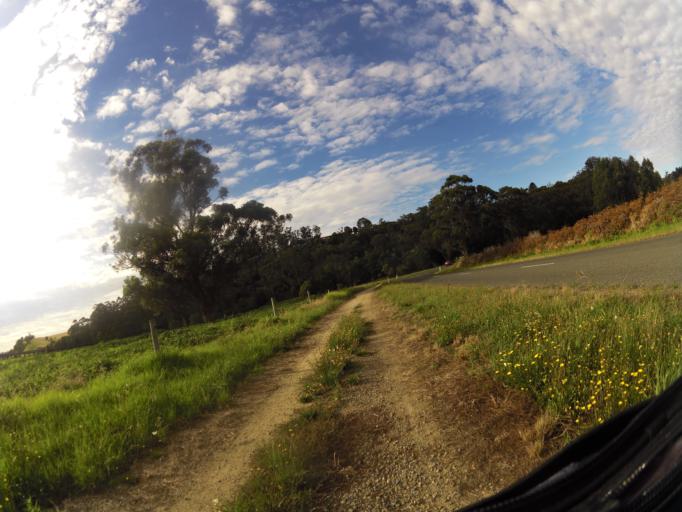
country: AU
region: Victoria
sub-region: East Gippsland
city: Lakes Entrance
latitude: -37.7259
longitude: 148.4403
